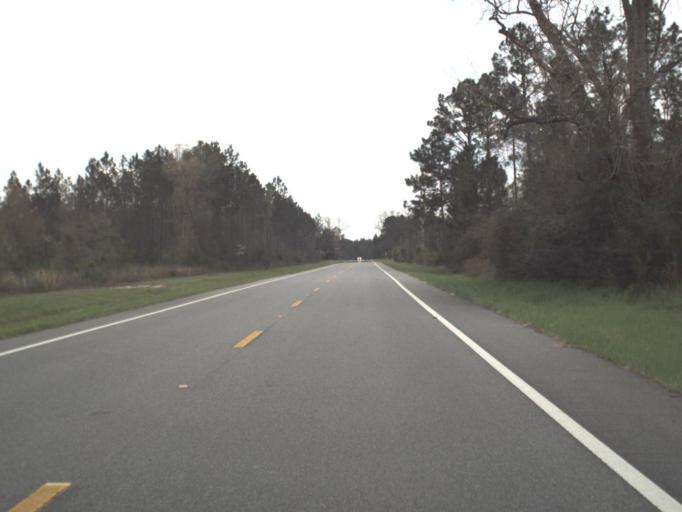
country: US
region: Florida
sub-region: Gulf County
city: Wewahitchka
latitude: 30.2559
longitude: -85.2331
